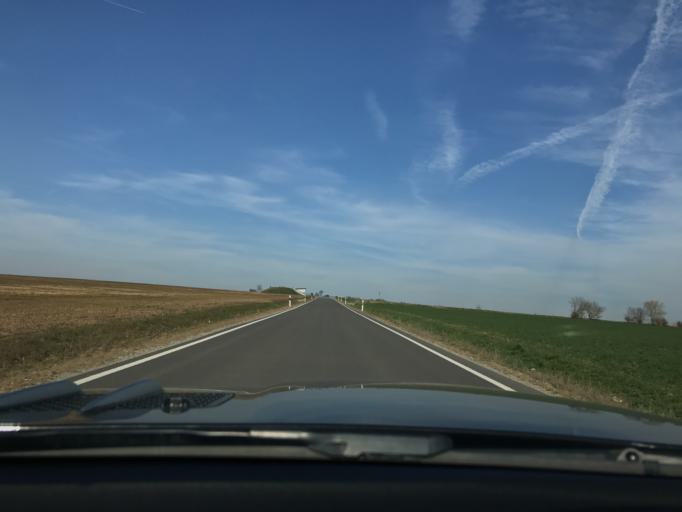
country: DE
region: Thuringia
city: Bothenheilingen
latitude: 51.1921
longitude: 10.6302
